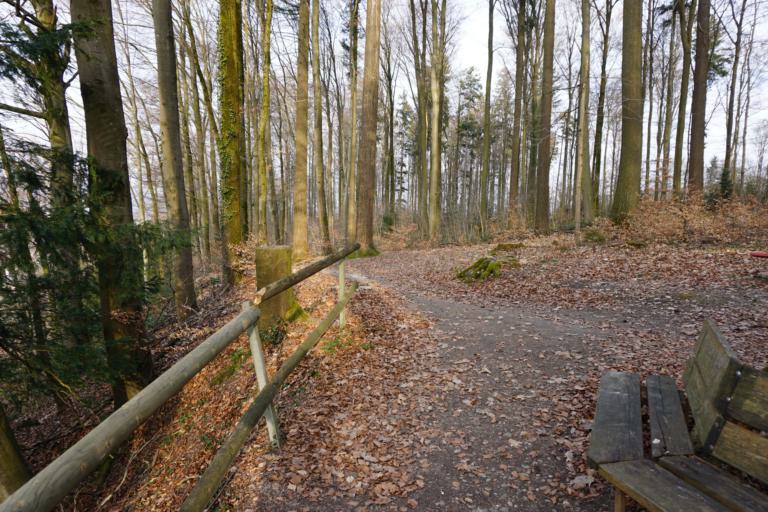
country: CH
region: Aargau
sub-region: Bezirk Aarau
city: Aarau
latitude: 47.3839
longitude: 8.0349
